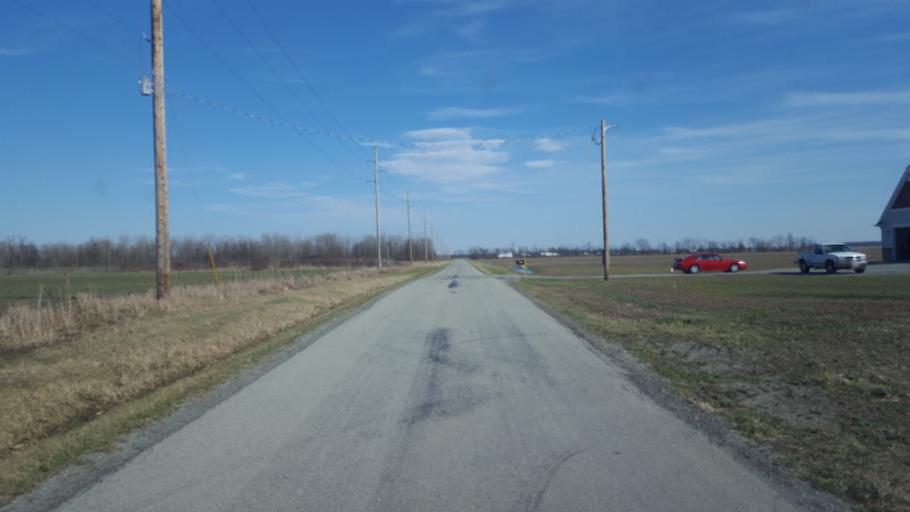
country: US
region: Ohio
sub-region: Wyandot County
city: Upper Sandusky
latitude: 40.6944
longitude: -83.3146
